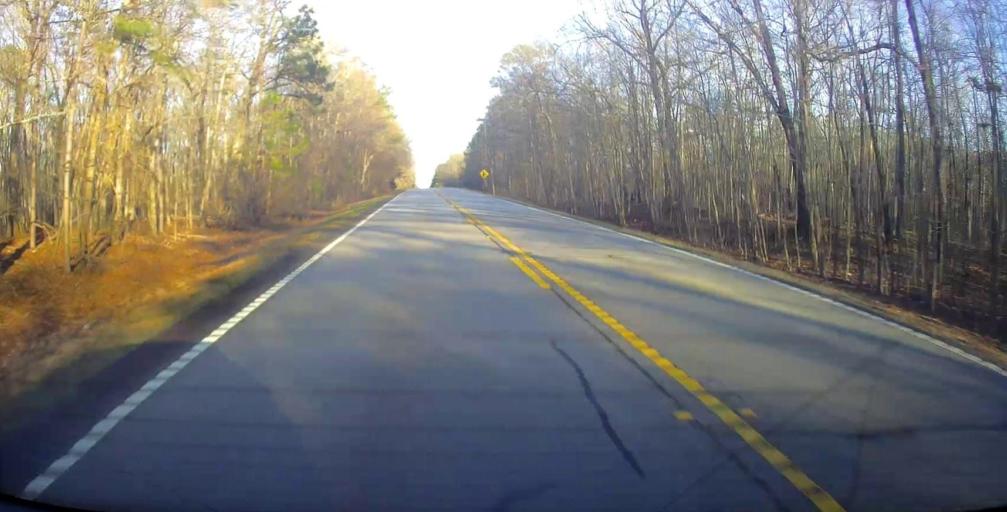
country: US
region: Georgia
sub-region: Harris County
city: Pine Mountain
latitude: 32.8555
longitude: -84.9637
